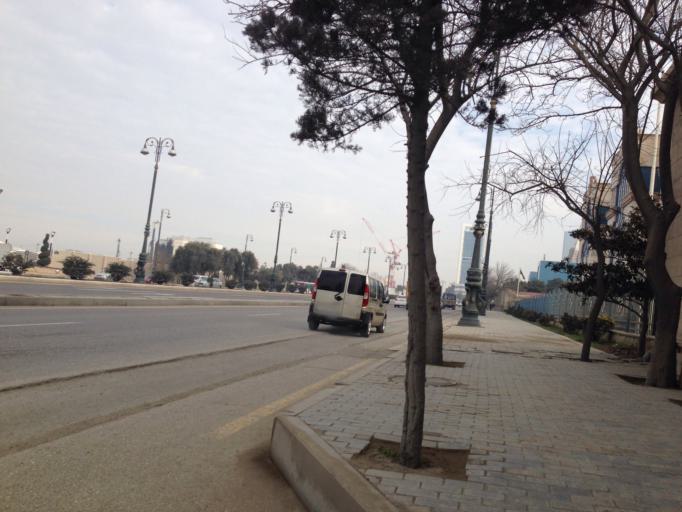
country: AZ
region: Baki
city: Baku
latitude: 40.4097
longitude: 49.8937
